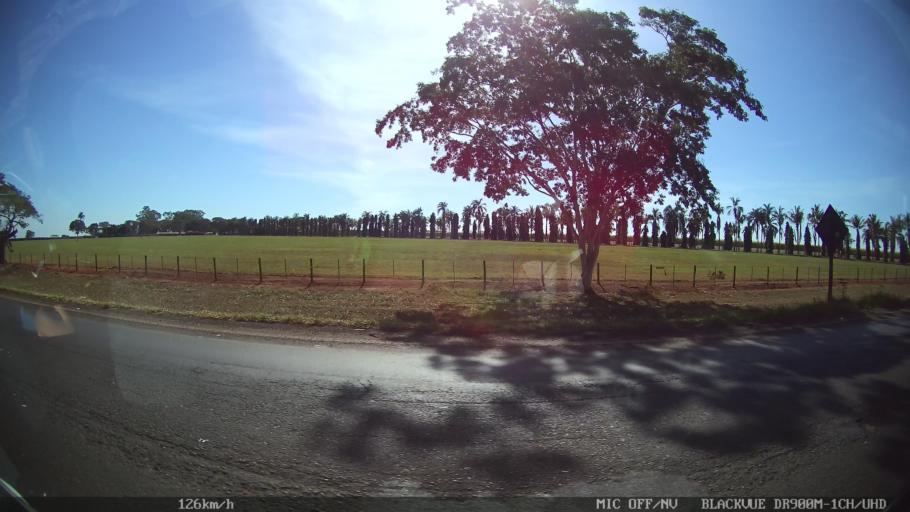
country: BR
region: Sao Paulo
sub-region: Barretos
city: Barretos
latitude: -20.5676
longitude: -48.6651
